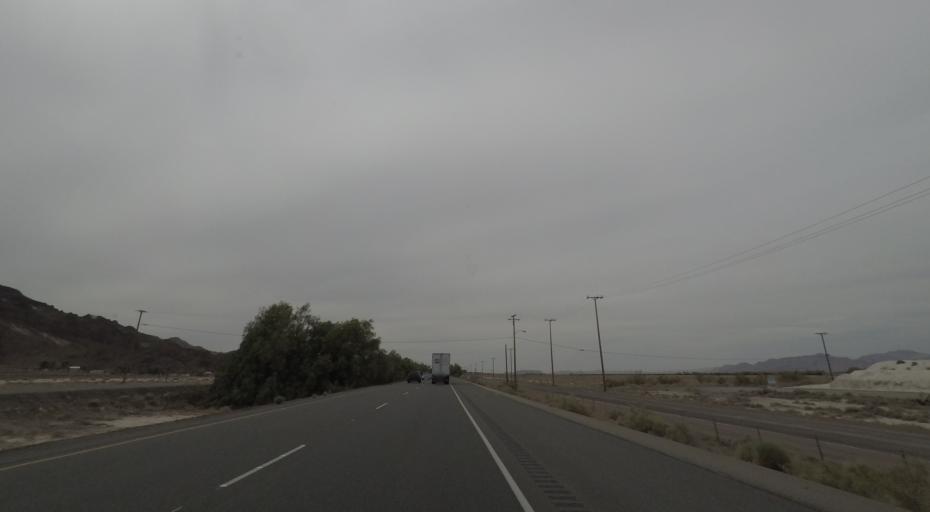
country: US
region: California
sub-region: San Bernardino County
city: Barstow
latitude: 34.8285
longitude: -116.6793
